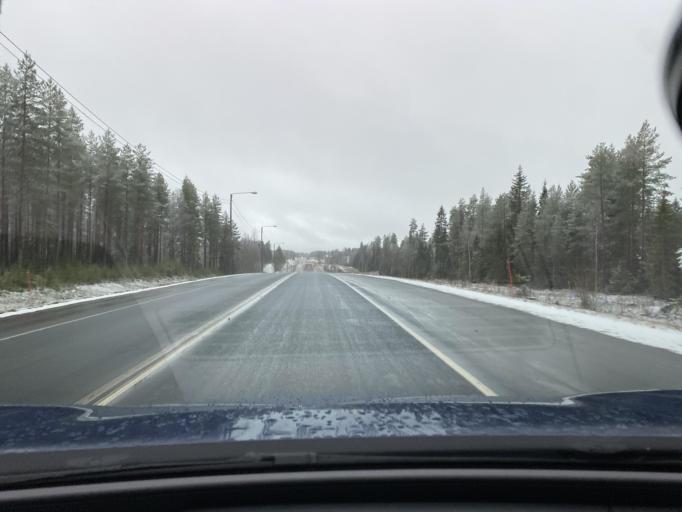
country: FI
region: Northern Ostrobothnia
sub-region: Oulu
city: Kiiminki
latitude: 65.1227
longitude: 25.7549
